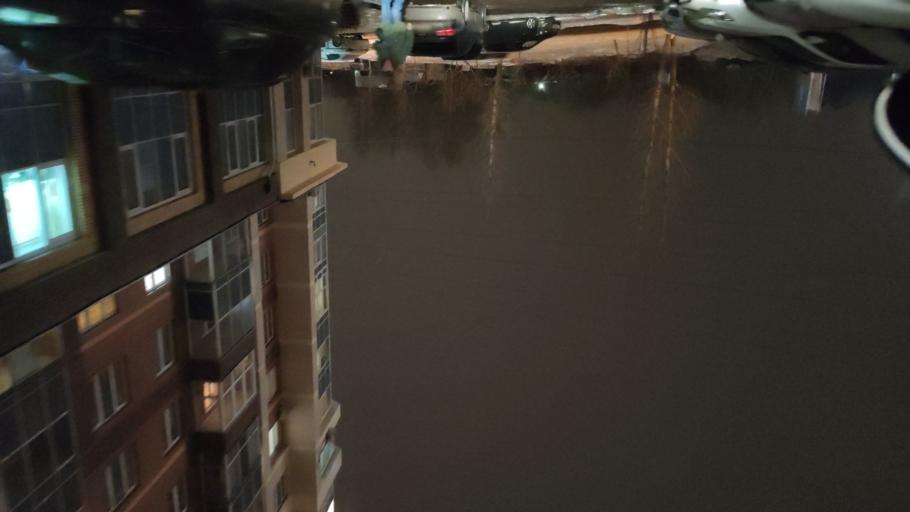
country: RU
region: Moskovskaya
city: Odintsovo
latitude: 55.6816
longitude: 37.2516
